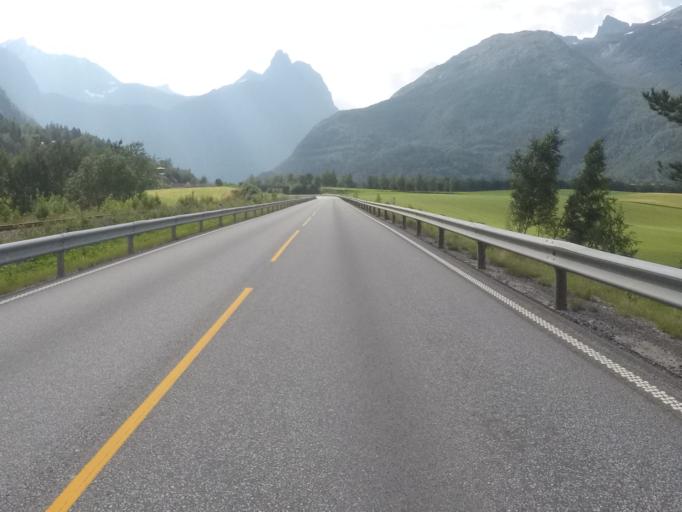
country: NO
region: More og Romsdal
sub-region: Rauma
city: Andalsnes
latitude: 62.5429
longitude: 7.7197
